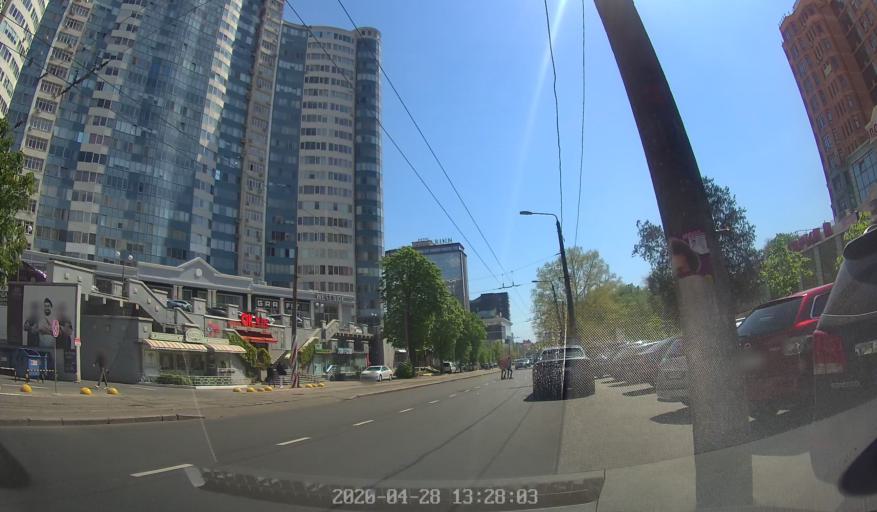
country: NG
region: Niger
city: Lemu
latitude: 9.2869
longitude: 6.1519
